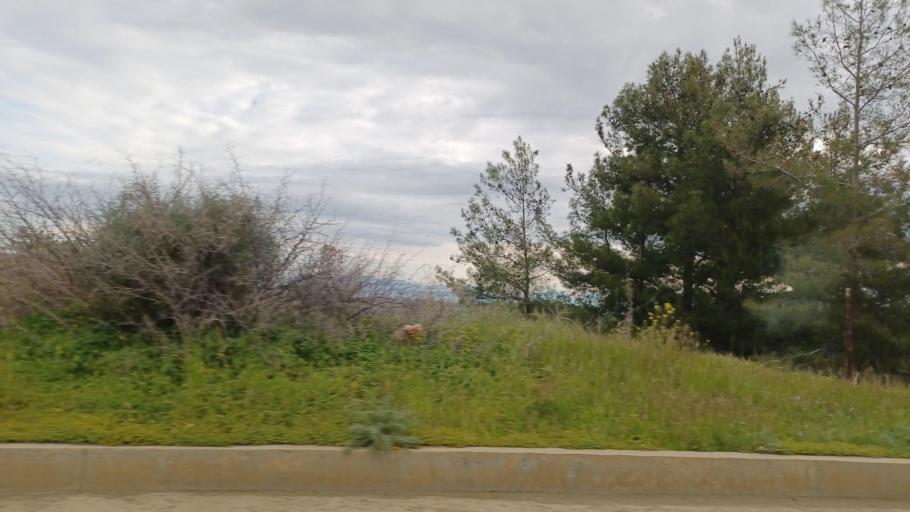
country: CY
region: Lefkosia
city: Lefka
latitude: 35.0792
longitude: 32.8952
